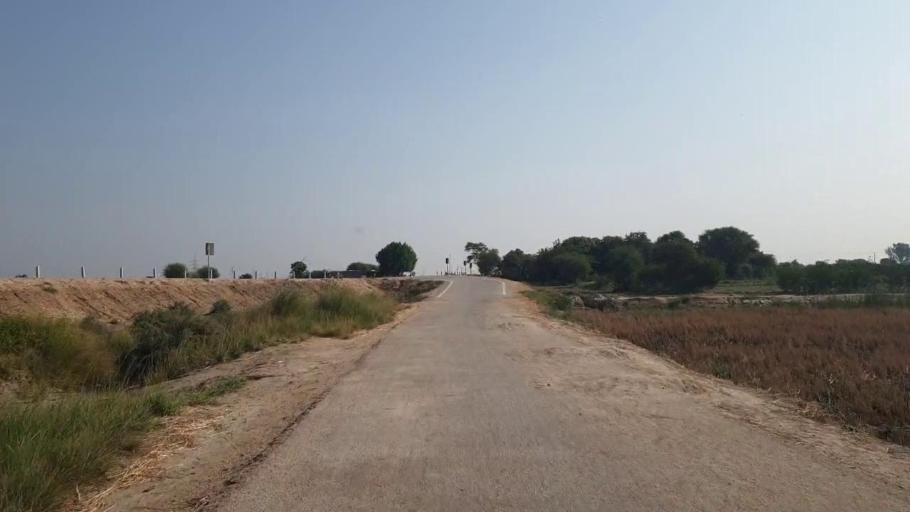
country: PK
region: Sindh
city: Matli
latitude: 24.9648
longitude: 68.6805
